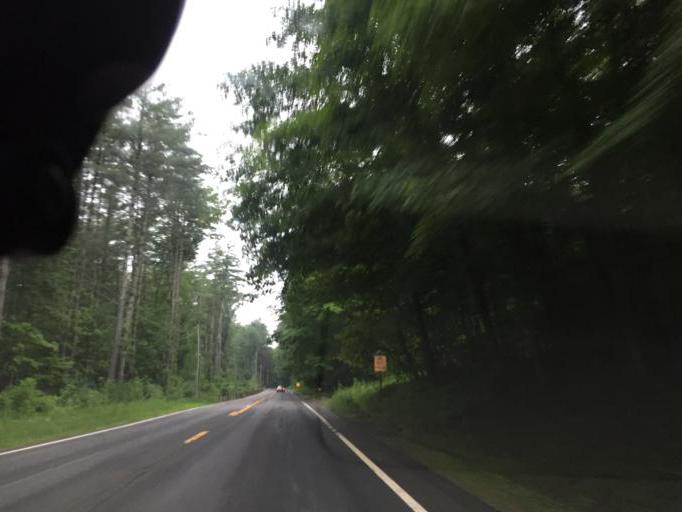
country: US
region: Connecticut
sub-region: Litchfield County
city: Canaan
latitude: 41.9436
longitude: -73.3101
